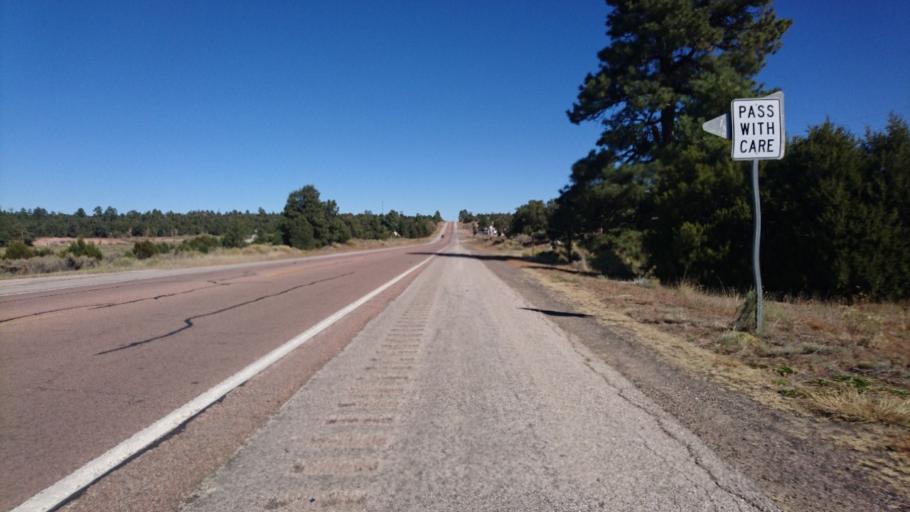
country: US
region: New Mexico
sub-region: McKinley County
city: Black Rock
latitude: 35.2367
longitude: -108.7639
